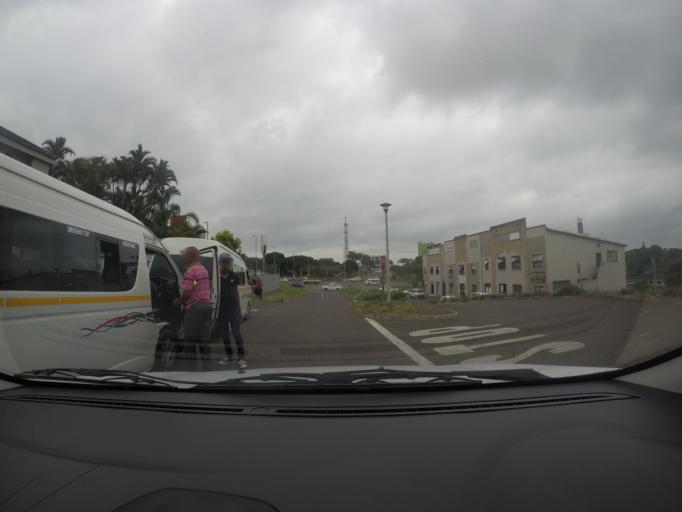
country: ZA
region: KwaZulu-Natal
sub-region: uThungulu District Municipality
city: Empangeni
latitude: -28.7469
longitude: 31.8901
